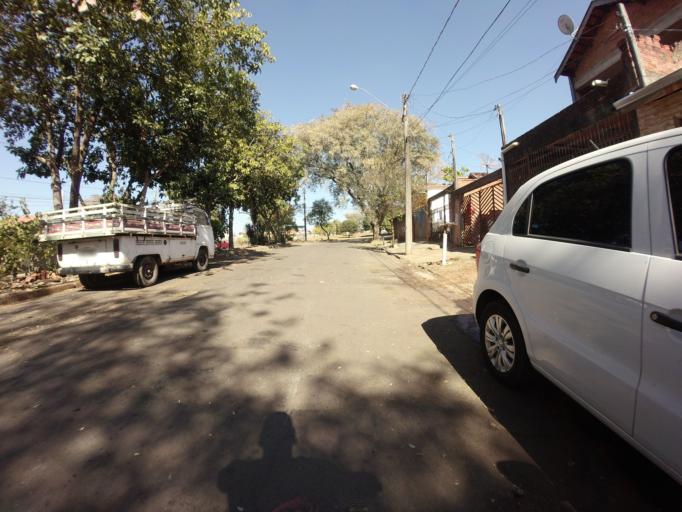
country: BR
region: Sao Paulo
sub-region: Piracicaba
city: Piracicaba
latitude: -22.7677
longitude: -47.5860
